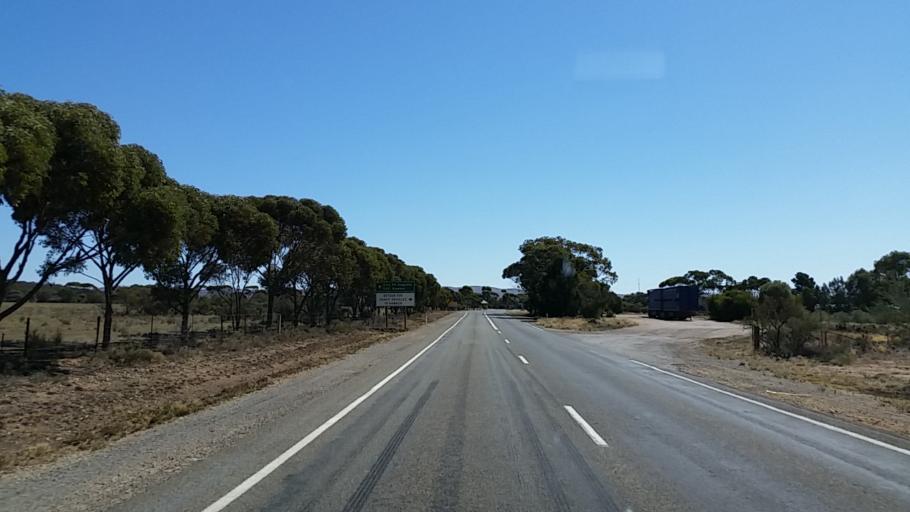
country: AU
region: South Australia
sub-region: Peterborough
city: Peterborough
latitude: -32.7402
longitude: 138.6236
